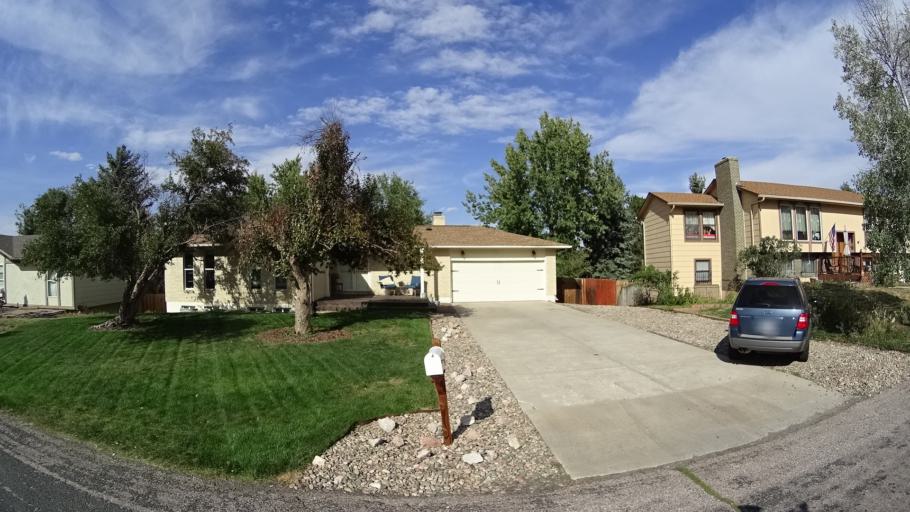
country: US
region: Colorado
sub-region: El Paso County
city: Colorado Springs
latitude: 38.8978
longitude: -104.7752
